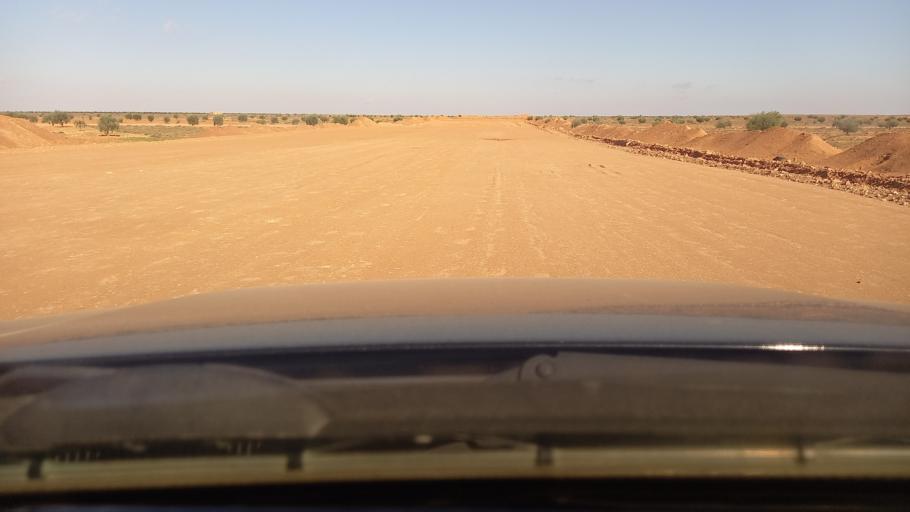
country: TN
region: Madanin
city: Medenine
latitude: 33.1760
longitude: 10.5284
